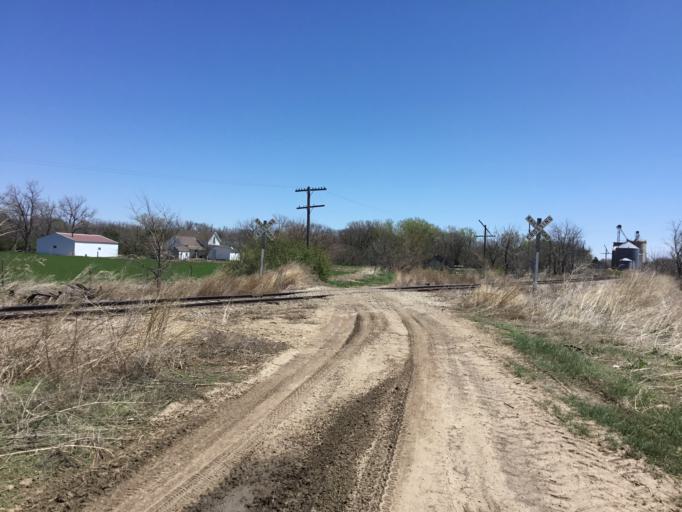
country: US
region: Kansas
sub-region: Phillips County
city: Phillipsburg
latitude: 39.7996
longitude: -99.4618
